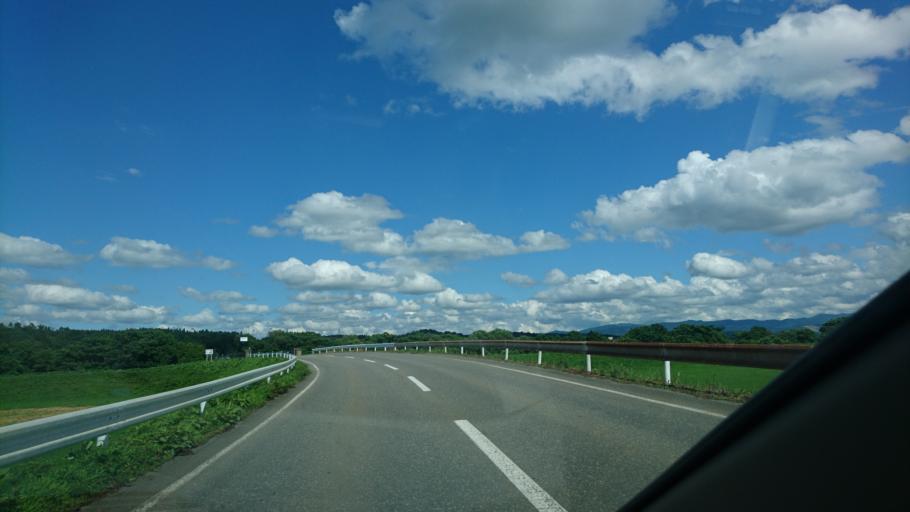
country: JP
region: Iwate
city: Mizusawa
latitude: 39.1999
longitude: 141.1594
